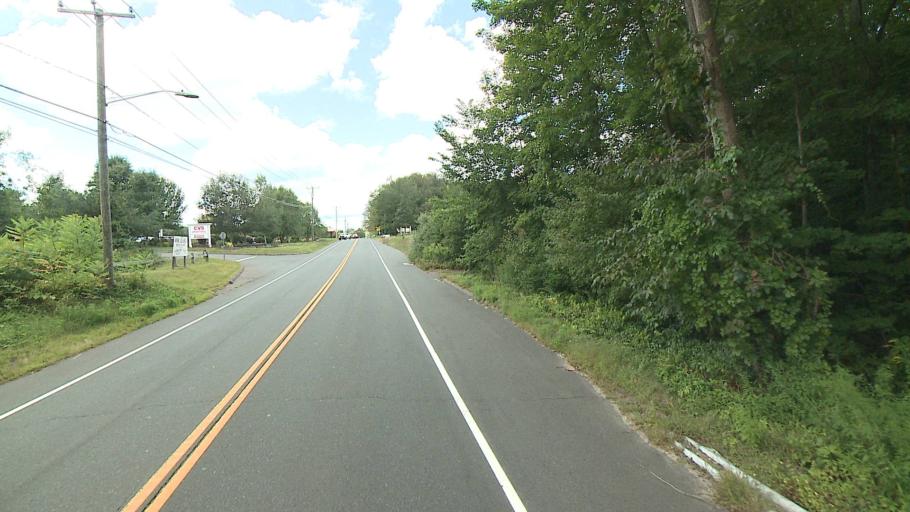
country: US
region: Connecticut
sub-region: Tolland County
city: Coventry Lake
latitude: 41.7985
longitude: -72.3678
